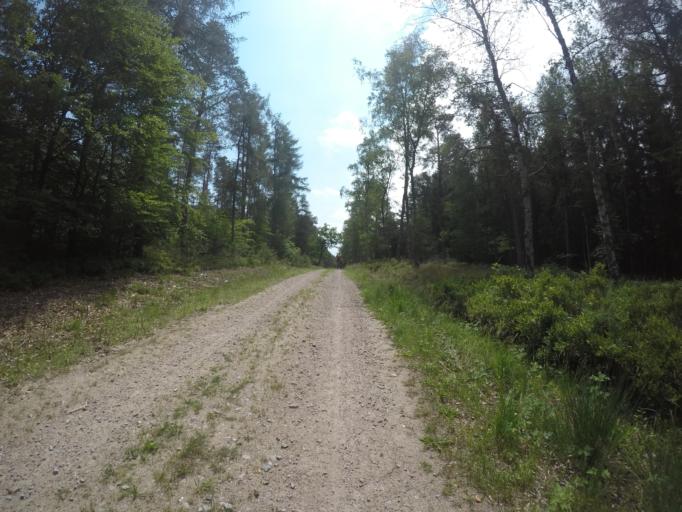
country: DE
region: Lower Saxony
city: Jesteburg
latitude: 53.2648
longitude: 9.9307
